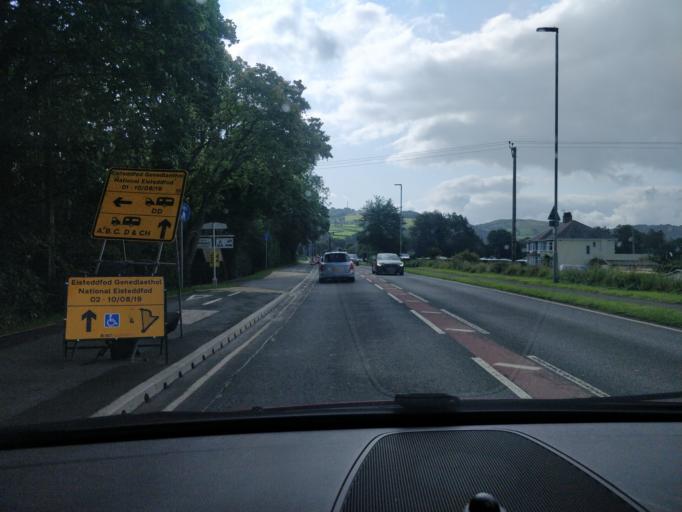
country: GB
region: Wales
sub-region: Conwy
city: Llanrwst
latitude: 53.1313
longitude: -3.7891
